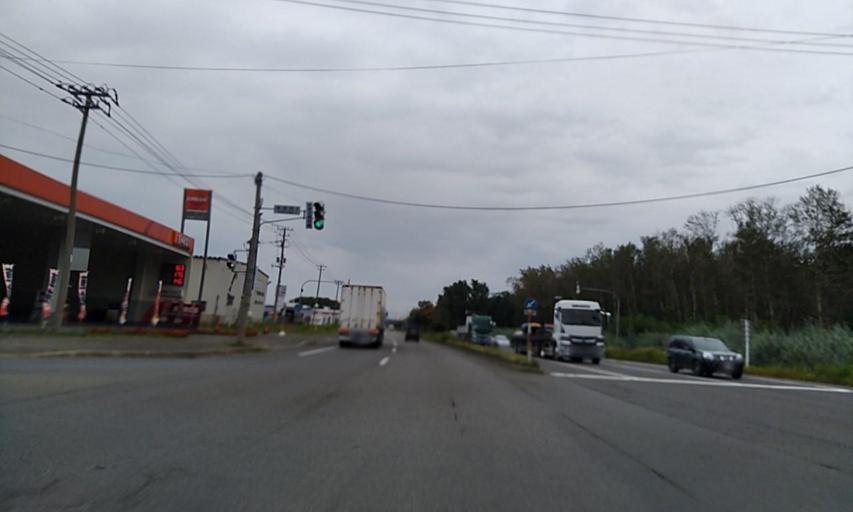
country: JP
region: Hokkaido
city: Ishikari
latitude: 43.1599
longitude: 141.2810
